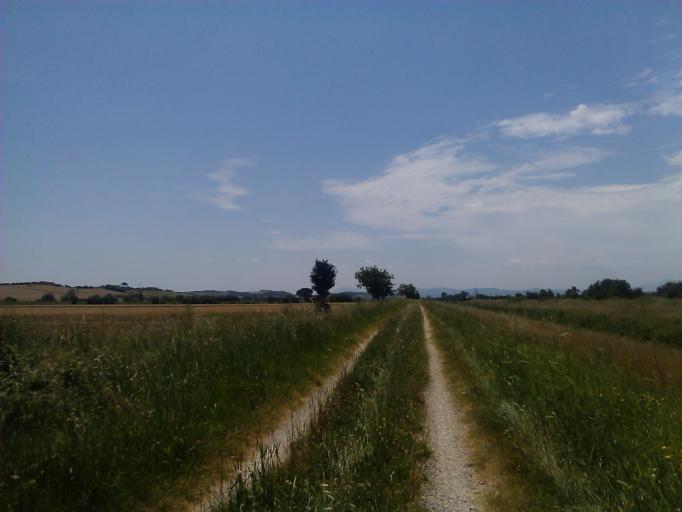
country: IT
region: Tuscany
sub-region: Province of Arezzo
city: Cesa
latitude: 43.2880
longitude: 11.8415
